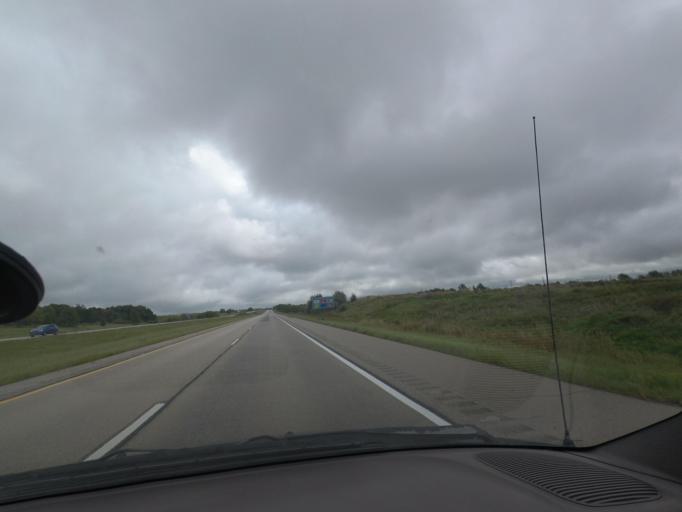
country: US
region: Illinois
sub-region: Piatt County
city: Monticello
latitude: 40.0309
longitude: -88.6260
